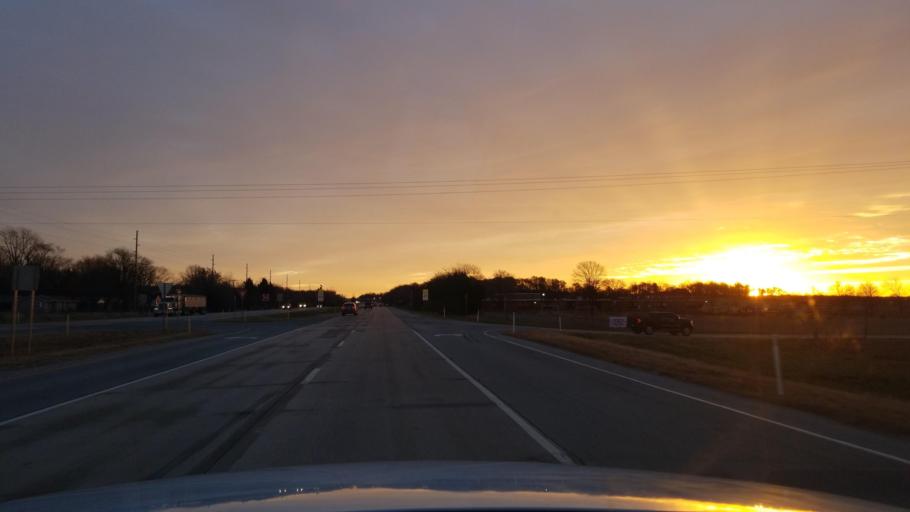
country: US
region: Indiana
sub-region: Posey County
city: Mount Vernon
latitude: 37.9418
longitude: -87.7559
